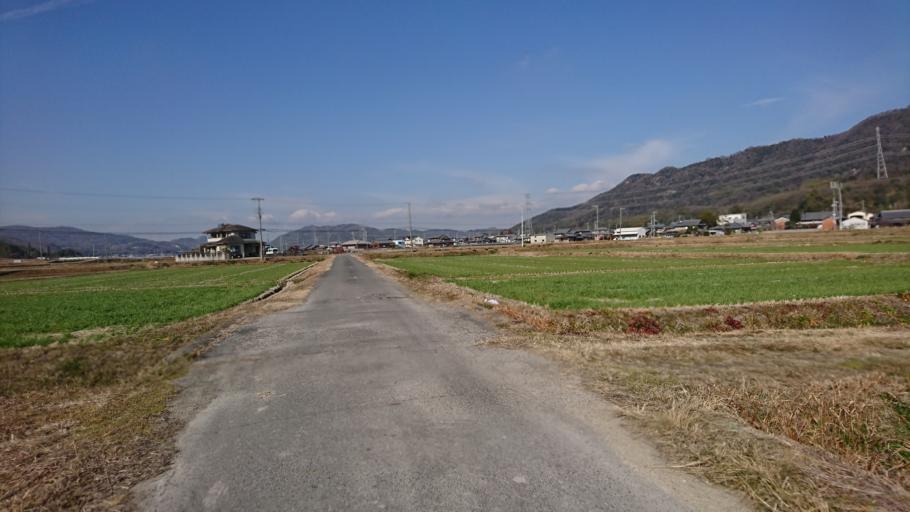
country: JP
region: Hyogo
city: Kakogawacho-honmachi
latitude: 34.8185
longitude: 134.8510
